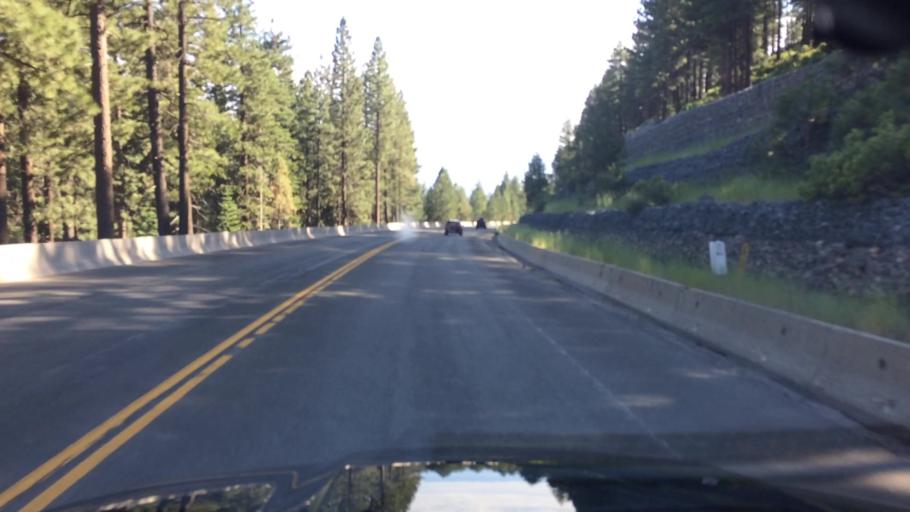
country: US
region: Nevada
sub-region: Washoe County
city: Incline Village
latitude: 39.2605
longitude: -119.9580
